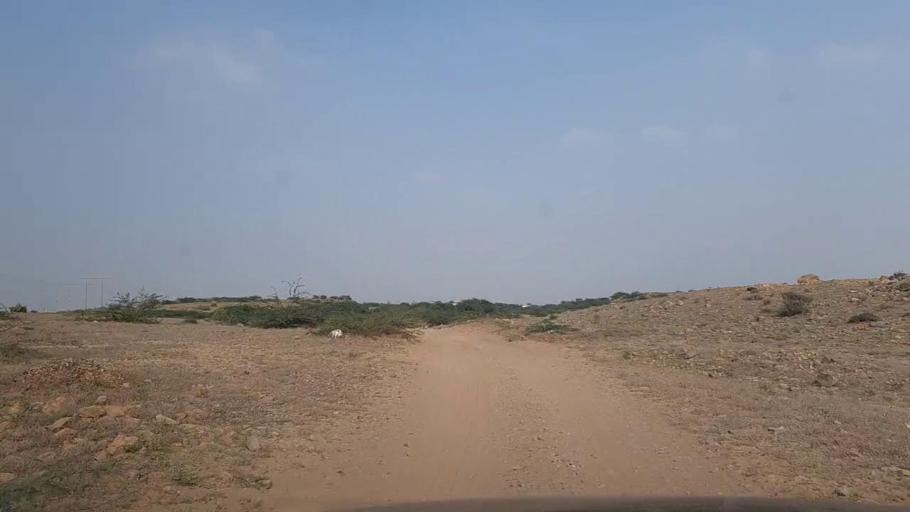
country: PK
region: Sindh
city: Thatta
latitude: 24.8887
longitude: 67.8428
